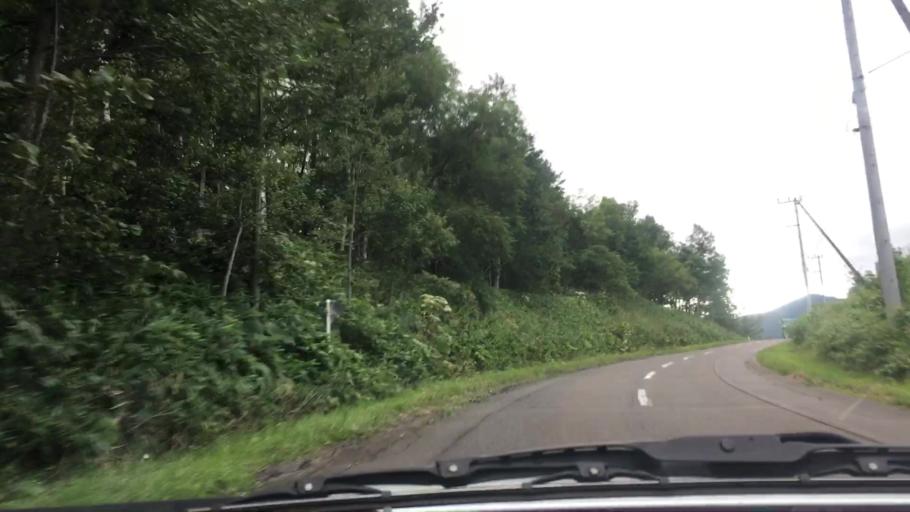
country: JP
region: Hokkaido
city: Otofuke
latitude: 43.1563
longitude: 142.8500
